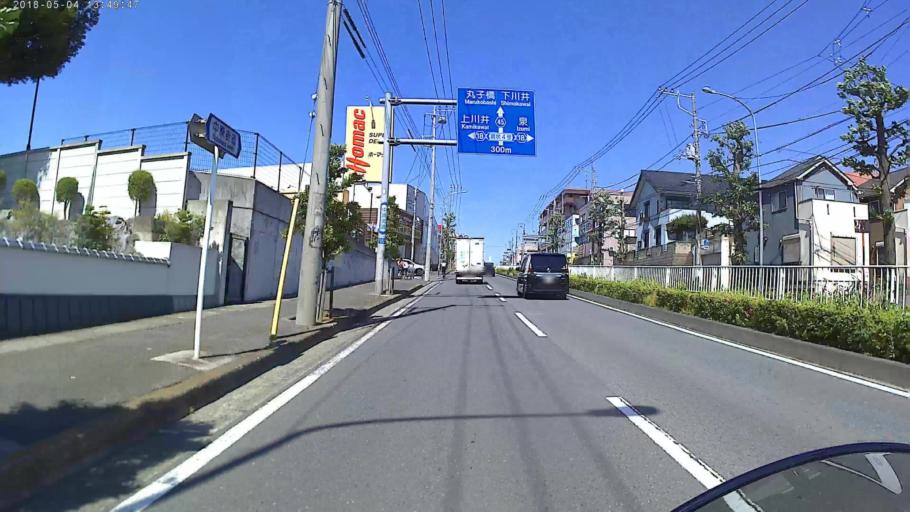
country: JP
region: Kanagawa
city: Minami-rinkan
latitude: 35.4572
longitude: 139.4784
